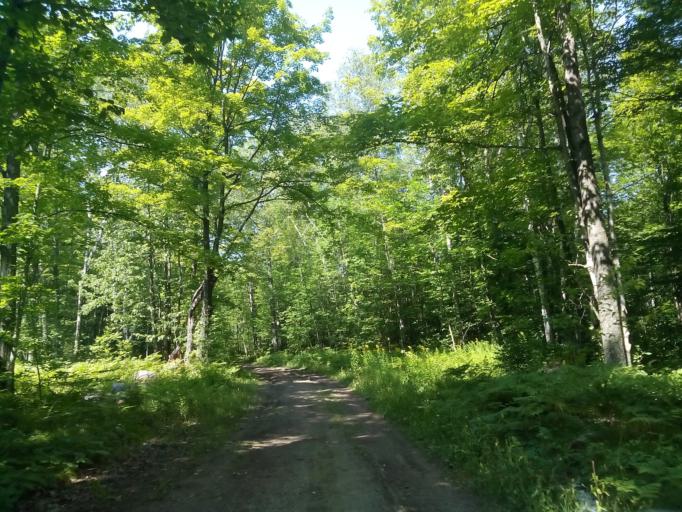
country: US
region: Wisconsin
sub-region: Forest County
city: Crandon
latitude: 45.3622
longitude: -88.5247
